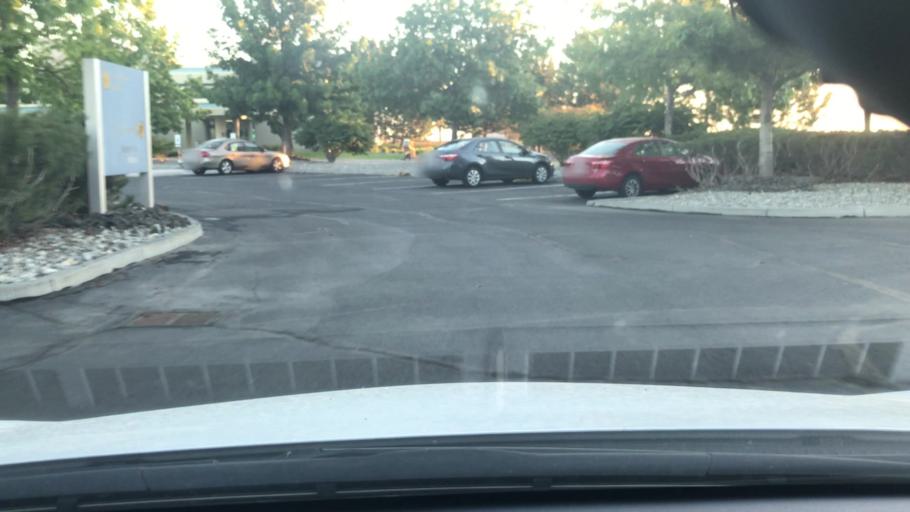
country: US
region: Washington
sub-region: Grant County
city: Moses Lake North
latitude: 47.1891
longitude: -119.3230
